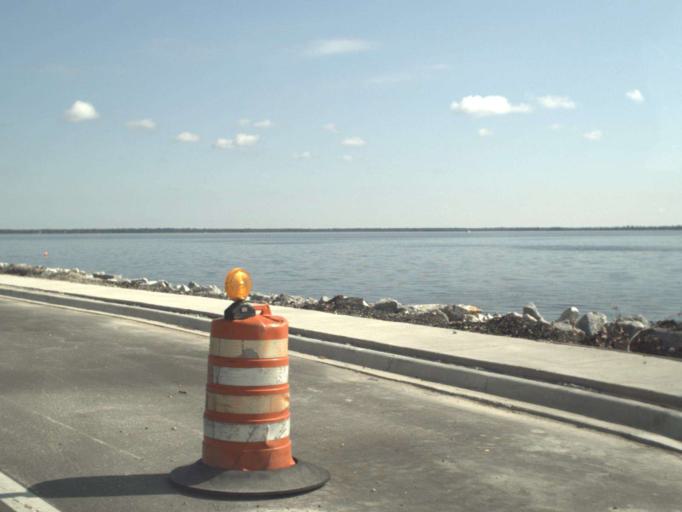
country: US
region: Florida
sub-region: Walton County
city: Seaside
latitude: 30.3910
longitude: -86.1728
